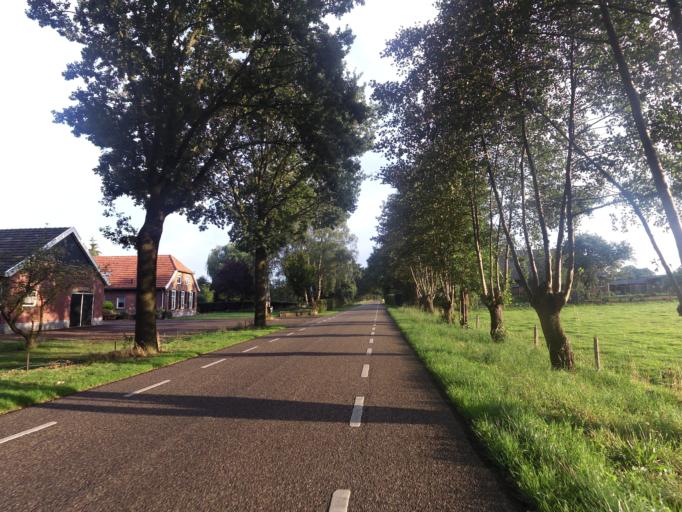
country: NL
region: Gelderland
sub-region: Oude IJsselstreek
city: Varsseveld
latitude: 51.9025
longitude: 6.4872
